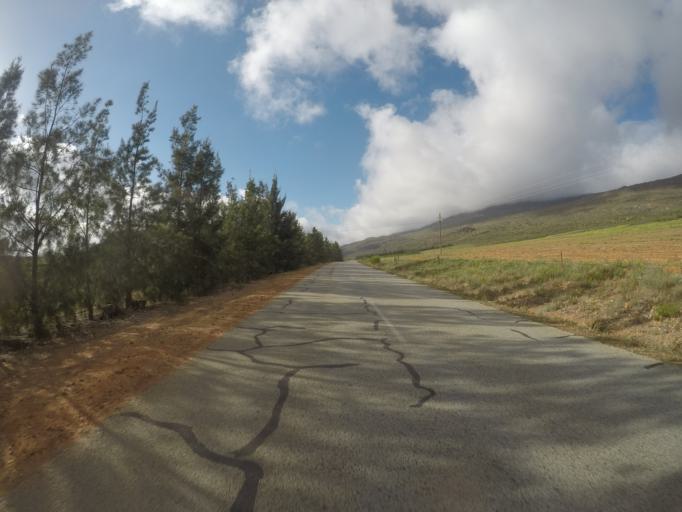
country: ZA
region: Western Cape
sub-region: West Coast District Municipality
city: Clanwilliam
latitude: -32.3504
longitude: 18.8476
